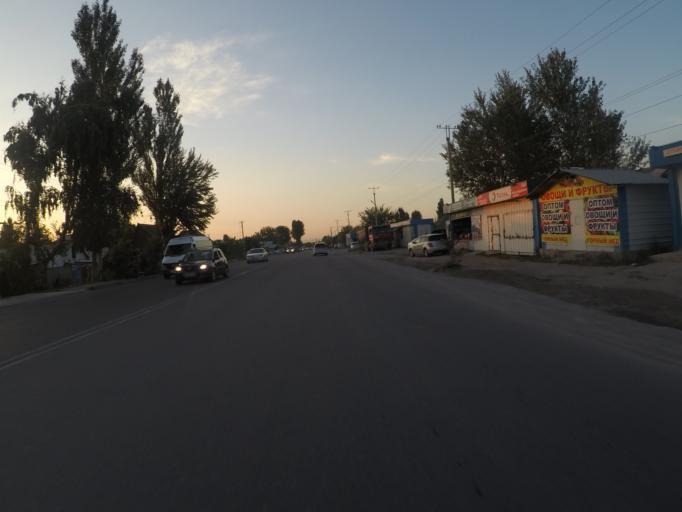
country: KG
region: Chuy
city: Lebedinovka
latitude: 42.8067
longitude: 74.6474
